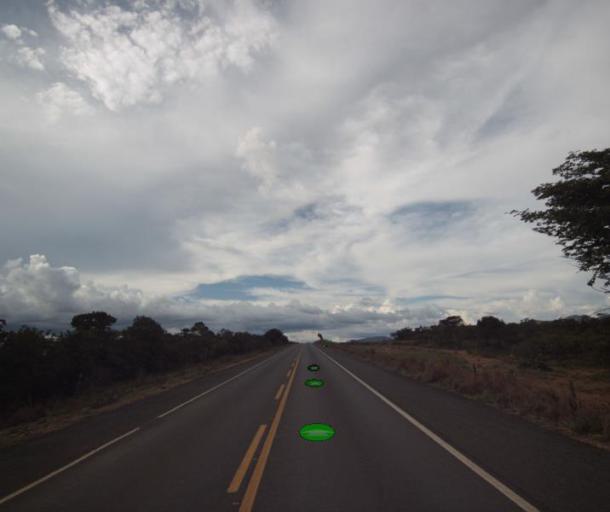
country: BR
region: Goias
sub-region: Niquelandia
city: Niquelandia
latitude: -14.7163
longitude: -48.6068
